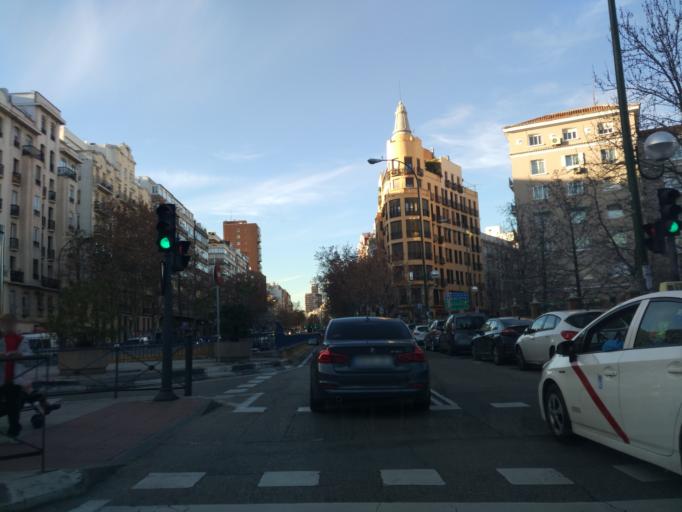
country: ES
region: Madrid
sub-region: Provincia de Madrid
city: Salamanca
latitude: 40.4299
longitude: -3.6703
